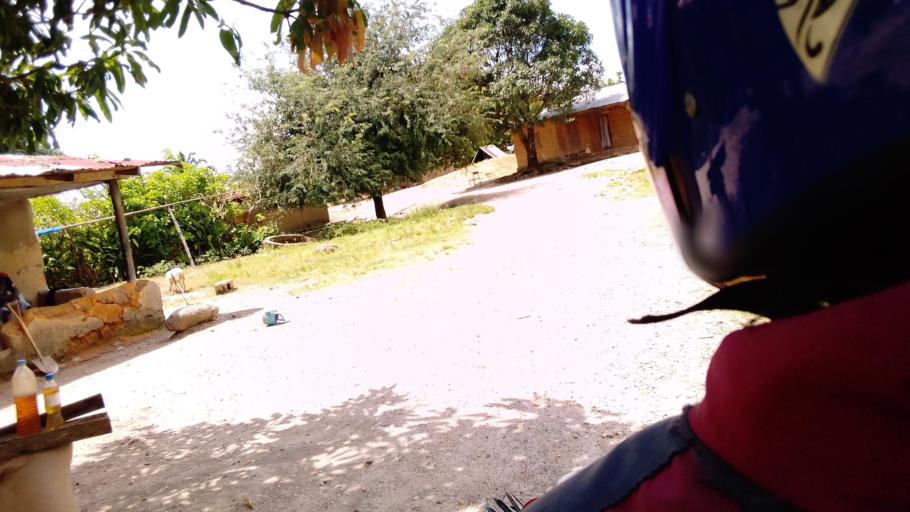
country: SL
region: Eastern Province
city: Koidu
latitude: 8.6742
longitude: -10.9960
